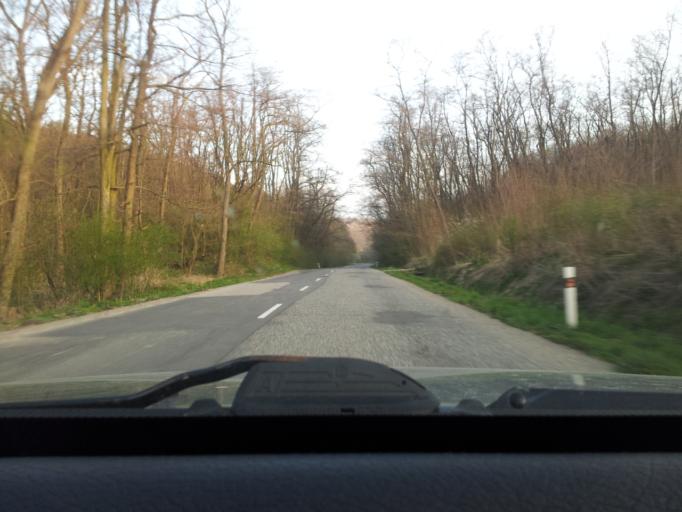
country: SK
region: Nitriansky
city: Tlmace
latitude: 48.2789
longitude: 18.4999
